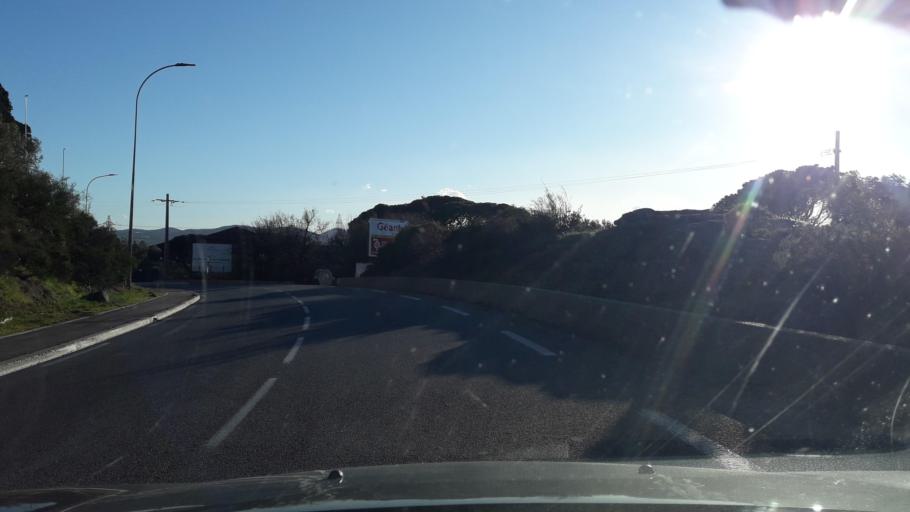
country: FR
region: Provence-Alpes-Cote d'Azur
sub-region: Departement du Var
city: Frejus
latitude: 43.4483
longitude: 6.7273
